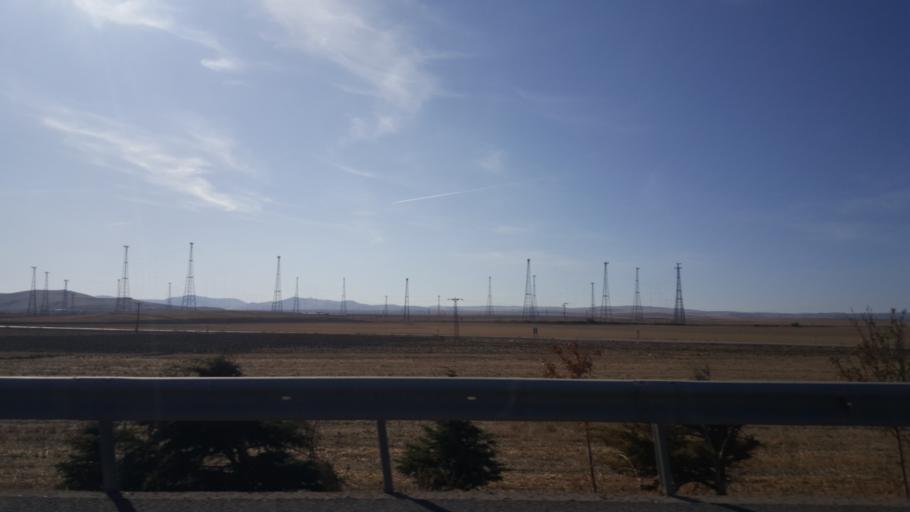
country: TR
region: Ankara
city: Yenice
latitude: 39.4081
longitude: 32.8707
